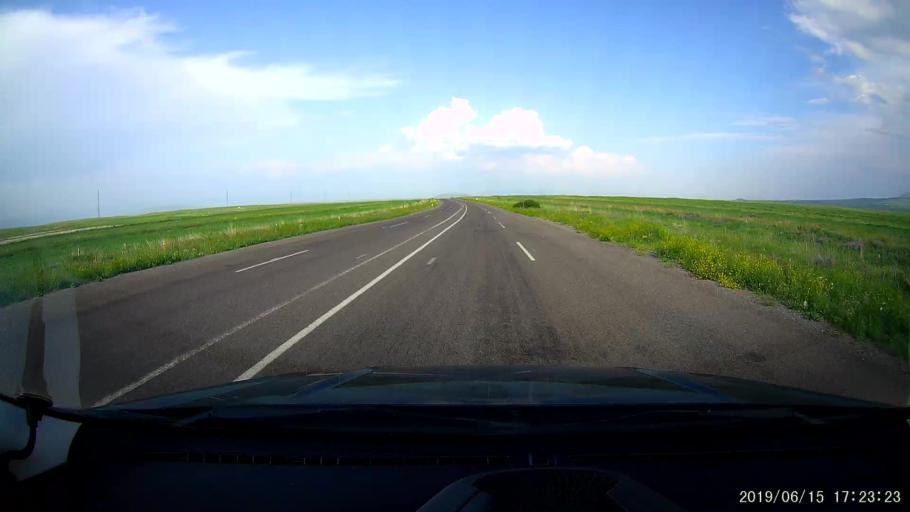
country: TR
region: Kars
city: Basgedikler
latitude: 40.6168
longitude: 43.3615
